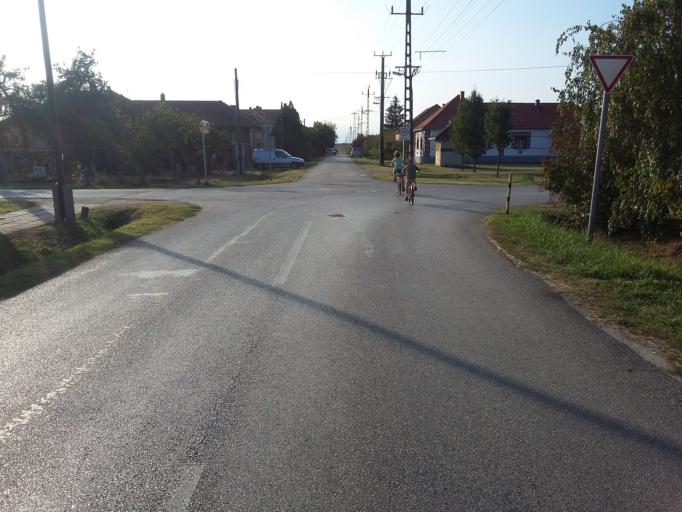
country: HU
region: Csongrad
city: Szeged
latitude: 46.2058
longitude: 20.1066
